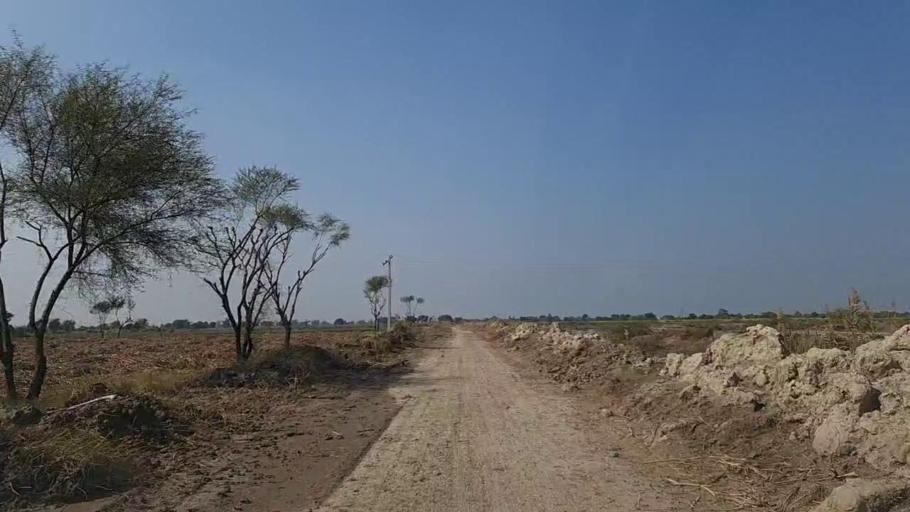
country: PK
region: Sindh
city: Nawabshah
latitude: 26.2901
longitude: 68.4851
